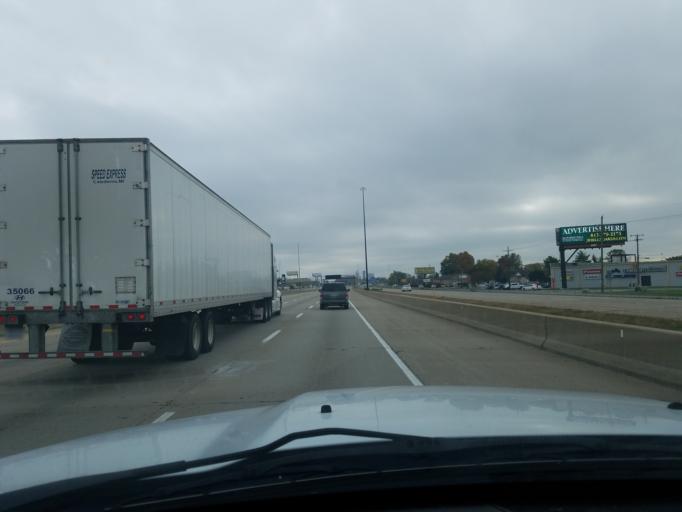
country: US
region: Indiana
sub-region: Clark County
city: Clarksville
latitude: 38.3073
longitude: -85.7526
